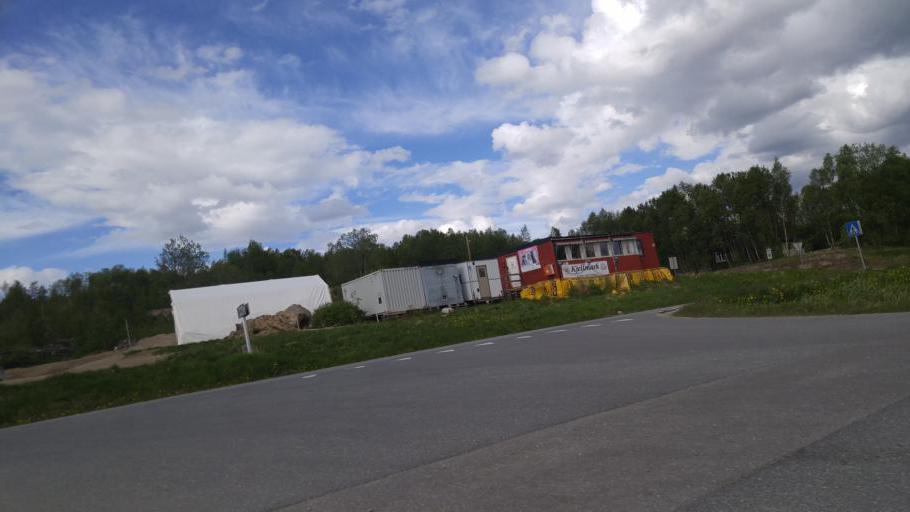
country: NO
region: Sor-Trondelag
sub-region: Roros
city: Roros
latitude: 62.5798
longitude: 11.3810
